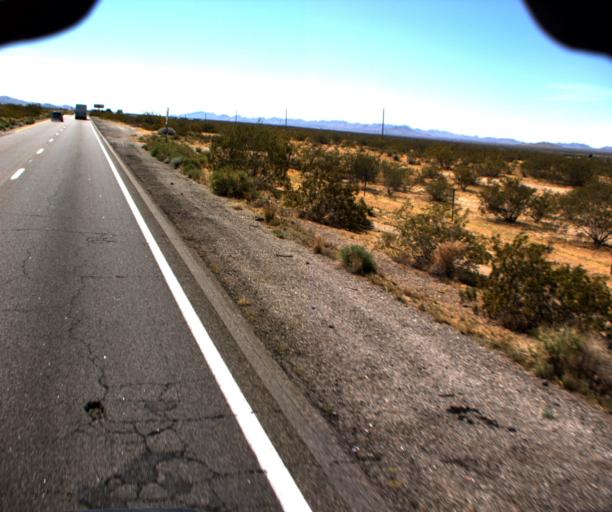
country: US
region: Arizona
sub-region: Mohave County
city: Dolan Springs
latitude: 35.5679
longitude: -114.3791
